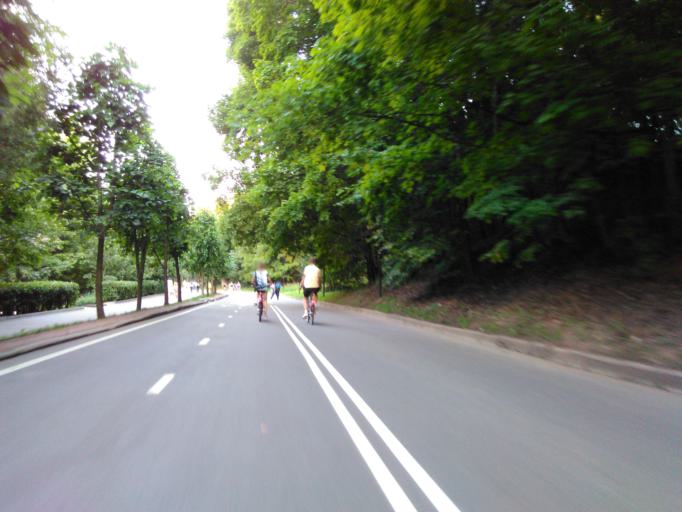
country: RU
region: Moscow
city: Luzhniki
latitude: 55.7107
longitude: 37.5484
